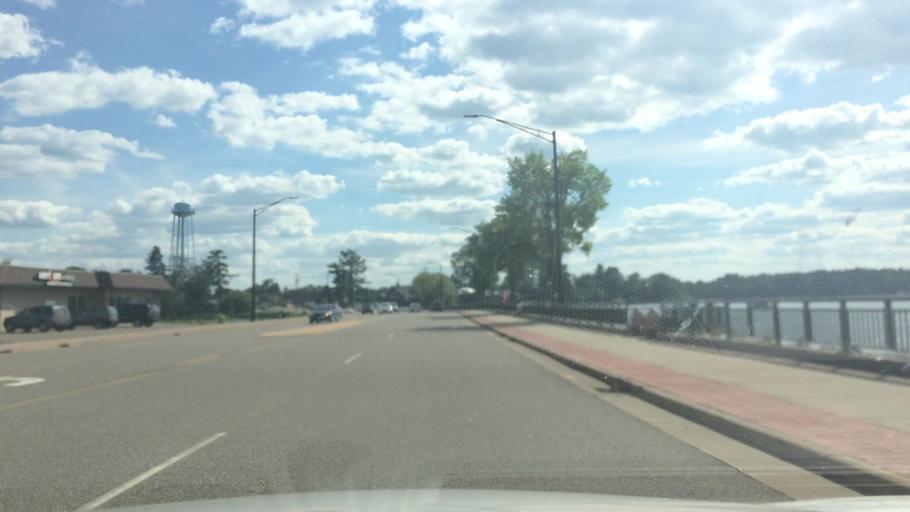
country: US
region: Wisconsin
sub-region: Vilas County
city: Lac du Flambeau
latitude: 45.8766
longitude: -89.7048
